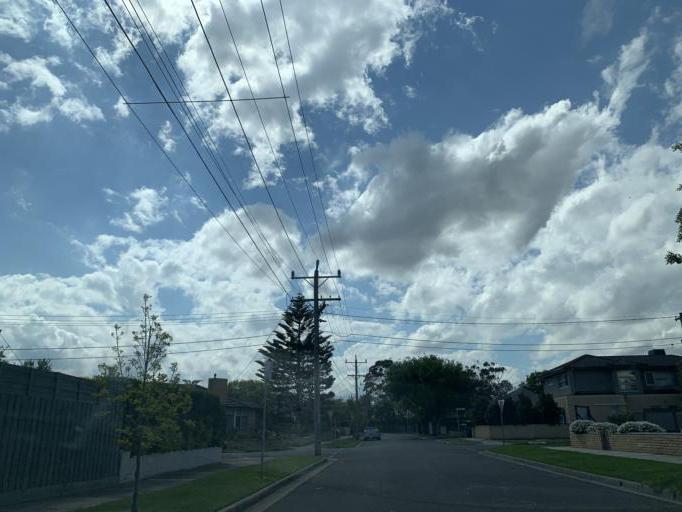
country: AU
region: Victoria
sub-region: Kingston
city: Mordialloc
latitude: -38.0019
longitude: 145.0919
